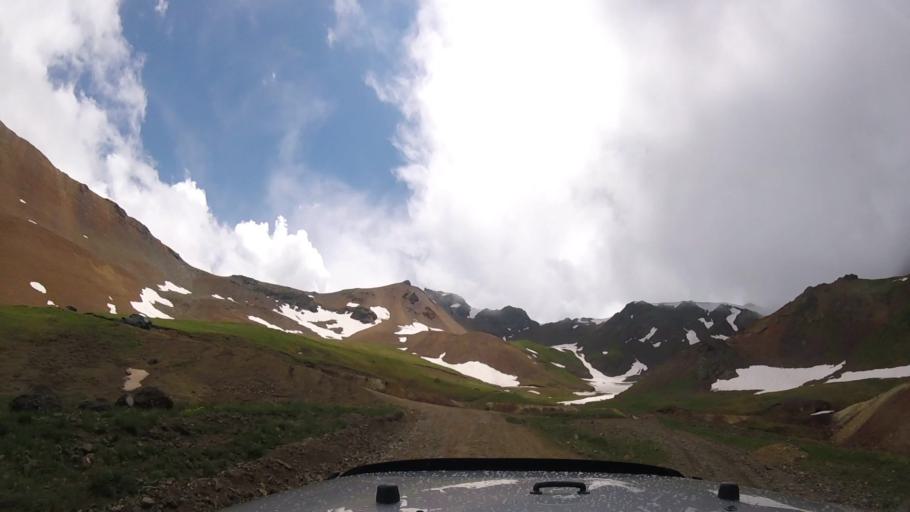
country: US
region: Colorado
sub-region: San Juan County
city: Silverton
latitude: 37.9169
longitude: -107.6127
